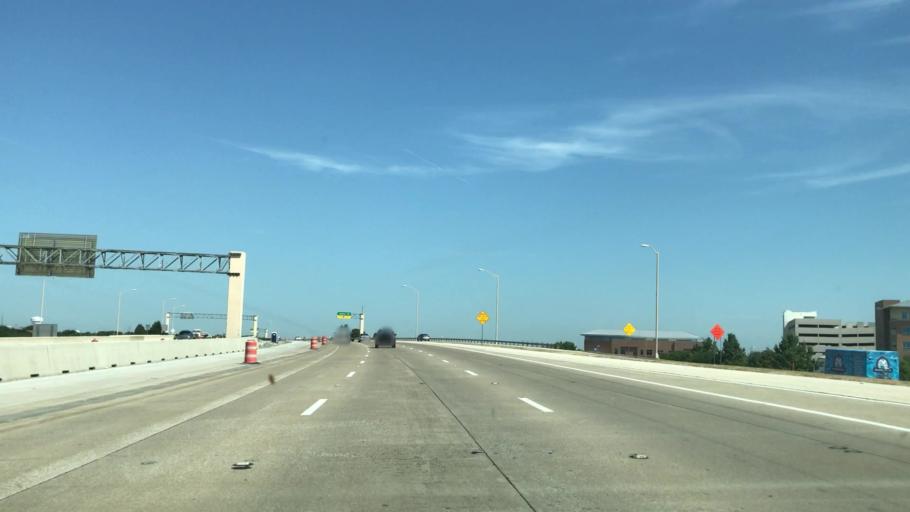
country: US
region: Texas
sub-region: Collin County
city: Plano
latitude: 32.9937
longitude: -96.6686
